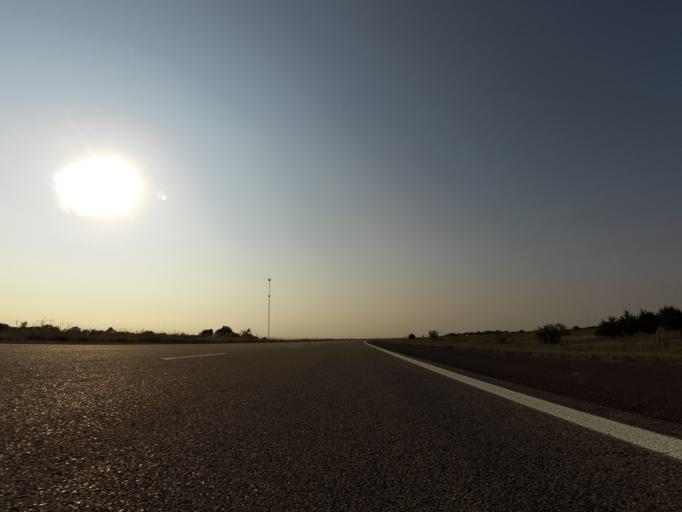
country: US
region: Kansas
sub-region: Reno County
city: South Hutchinson
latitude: 37.9687
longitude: -97.9325
